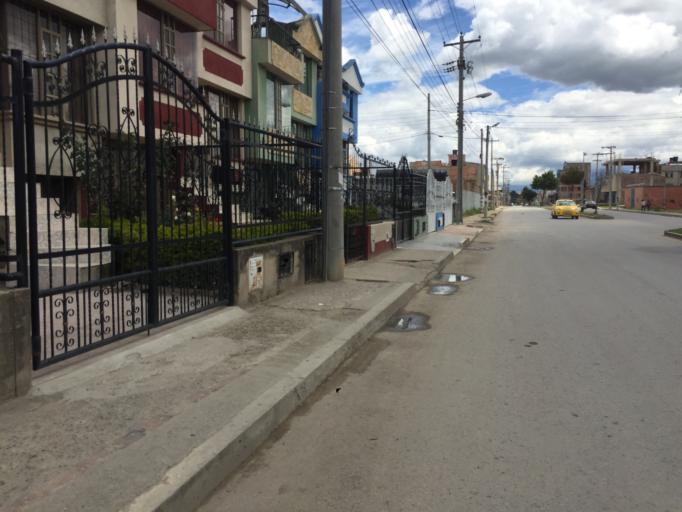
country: CO
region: Boyaca
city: Sogamoso
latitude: 5.7079
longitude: -72.9371
